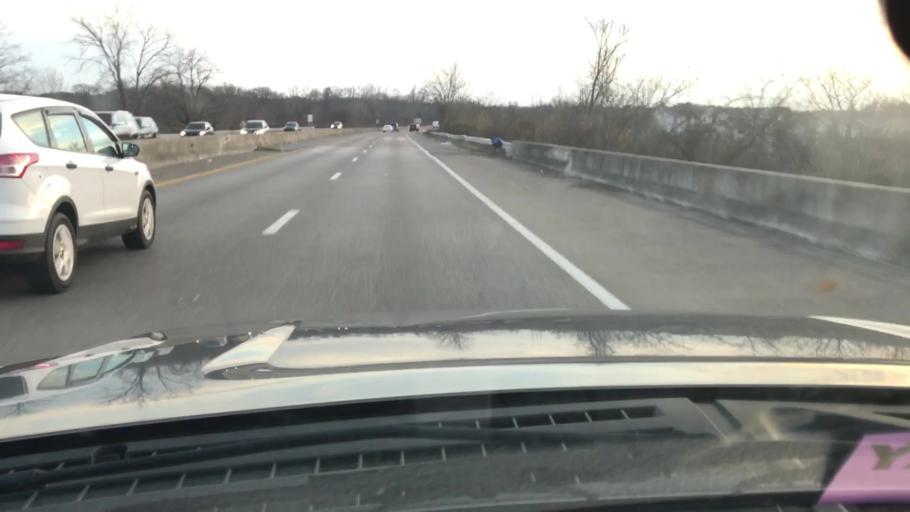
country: US
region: Tennessee
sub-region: Wilson County
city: Green Hill
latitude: 36.1741
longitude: -86.6061
